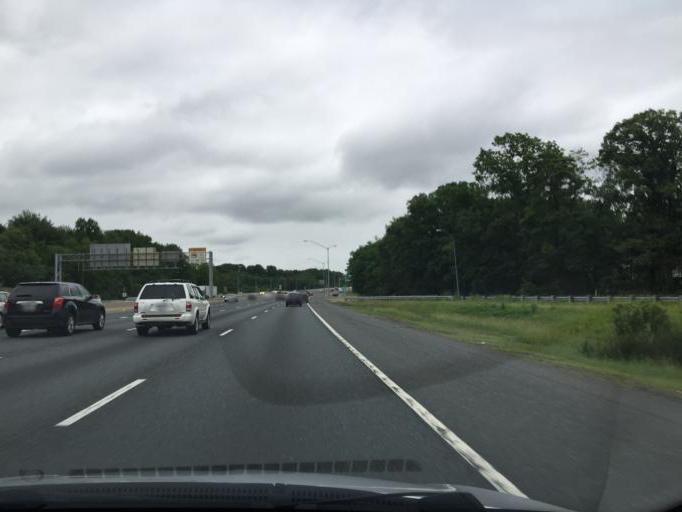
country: US
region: Maryland
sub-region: Baltimore County
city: Carney
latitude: 39.3873
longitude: -76.5282
